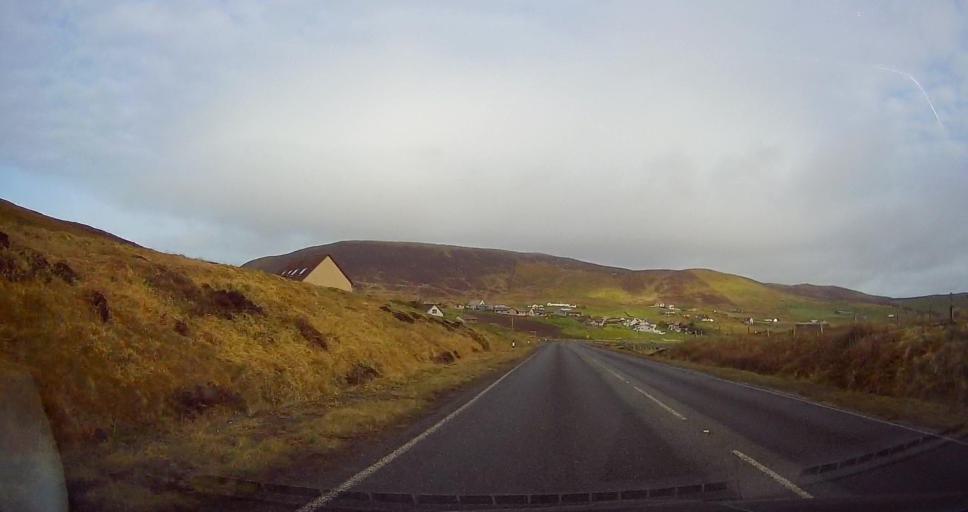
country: GB
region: Scotland
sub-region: Shetland Islands
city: Sandwick
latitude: 60.0942
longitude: -1.2306
